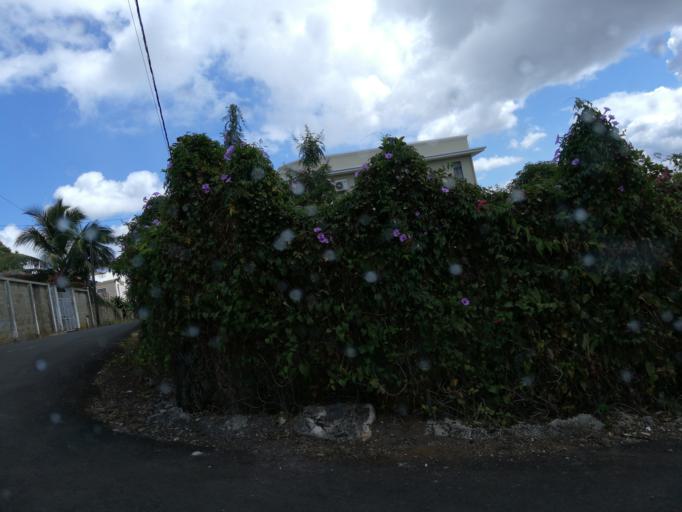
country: MU
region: Moka
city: Moka
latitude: -20.2138
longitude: 57.4739
